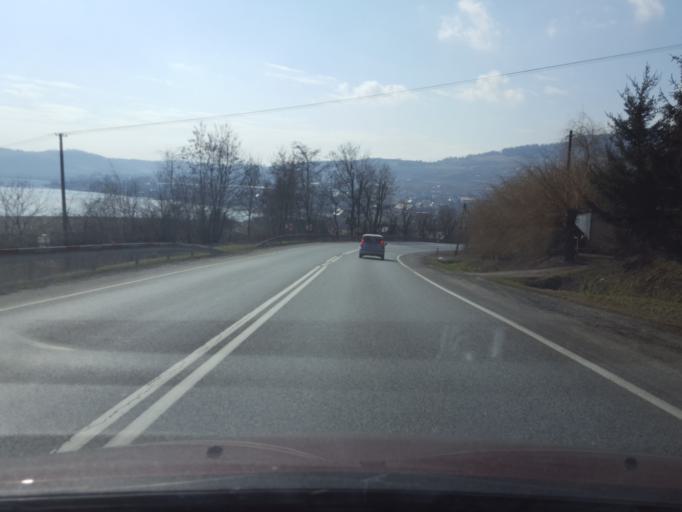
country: PL
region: Lesser Poland Voivodeship
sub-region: Powiat nowosadecki
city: Lososina Dolna
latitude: 49.7187
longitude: 20.6416
